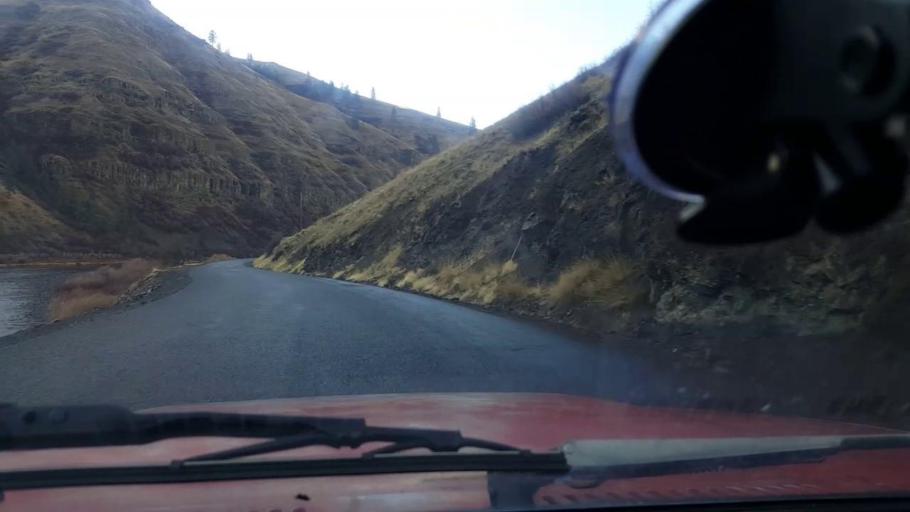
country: US
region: Washington
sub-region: Asotin County
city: Asotin
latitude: 46.0214
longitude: -117.3426
